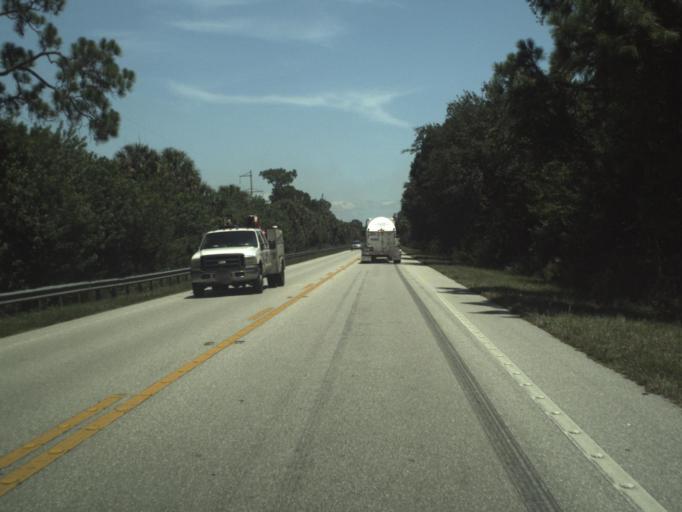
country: US
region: Florida
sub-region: Martin County
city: Indiantown
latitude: 27.1022
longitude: -80.5916
